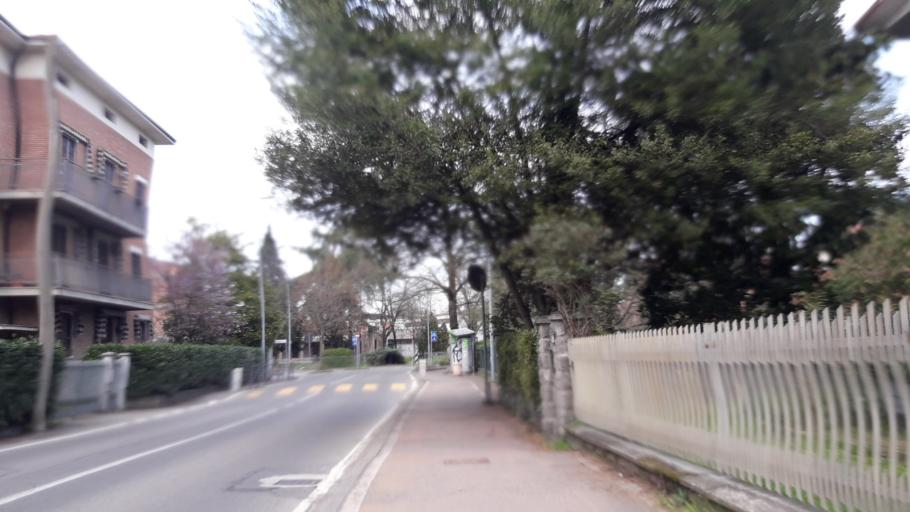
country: IT
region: Emilia-Romagna
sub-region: Provincia di Reggio Emilia
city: Reggio nell'Emilia
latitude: 44.6860
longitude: 10.6031
